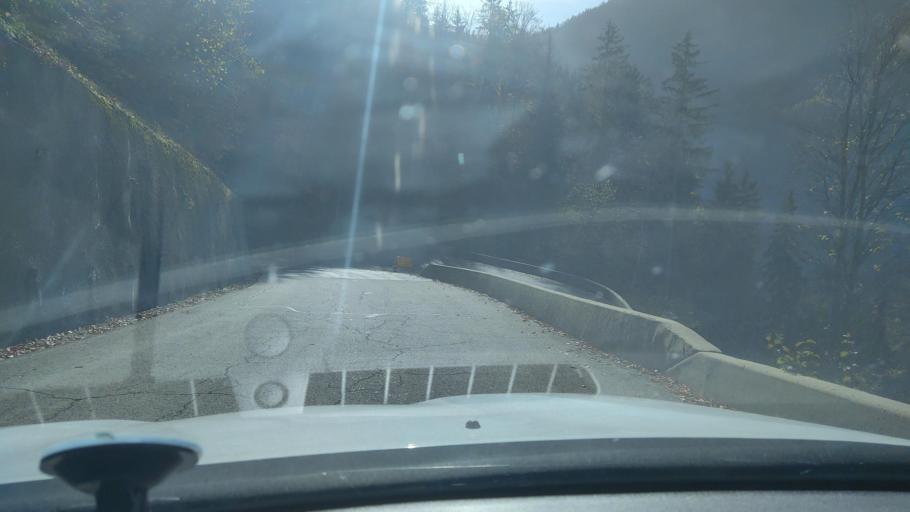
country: FR
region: Rhone-Alpes
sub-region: Departement de la Savoie
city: Saint-Jean-de-Maurienne
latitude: 45.2246
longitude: 6.3186
